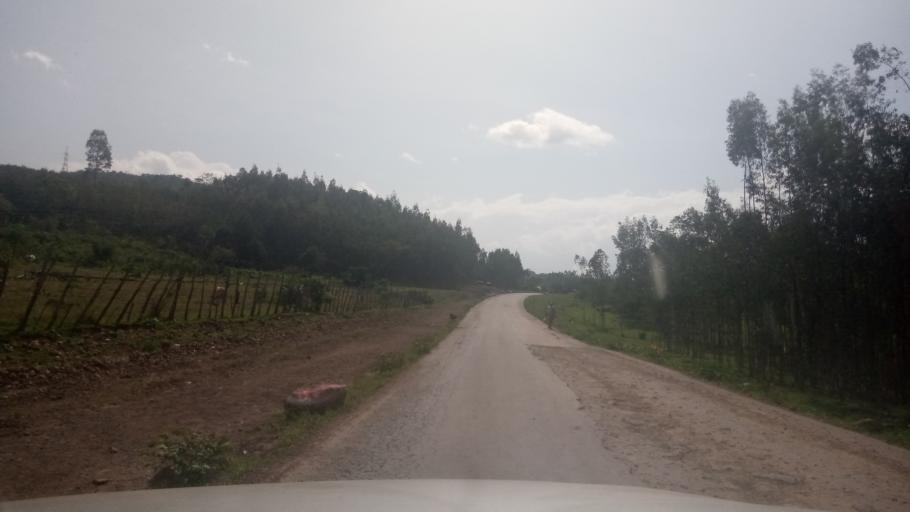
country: ET
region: Oromiya
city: Agaro
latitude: 7.9961
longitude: 36.5028
